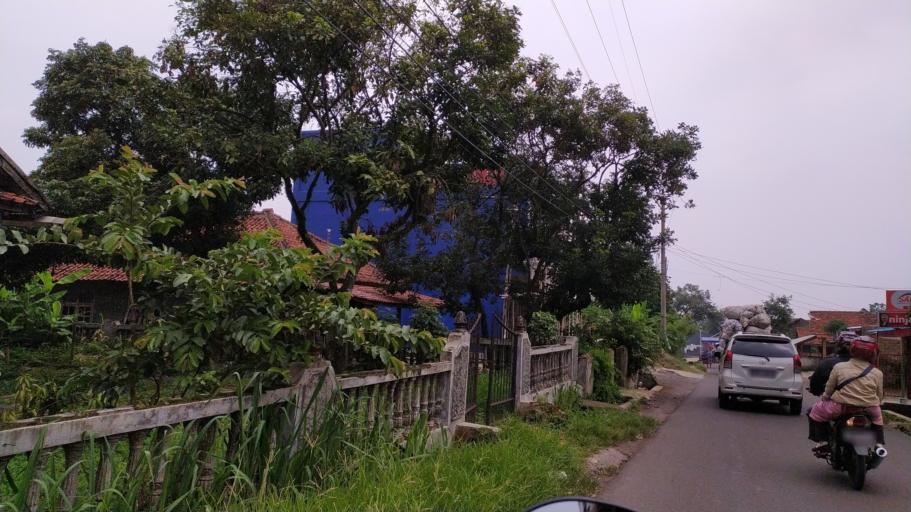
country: ID
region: West Java
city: Ciampea
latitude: -6.5965
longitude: 106.7045
